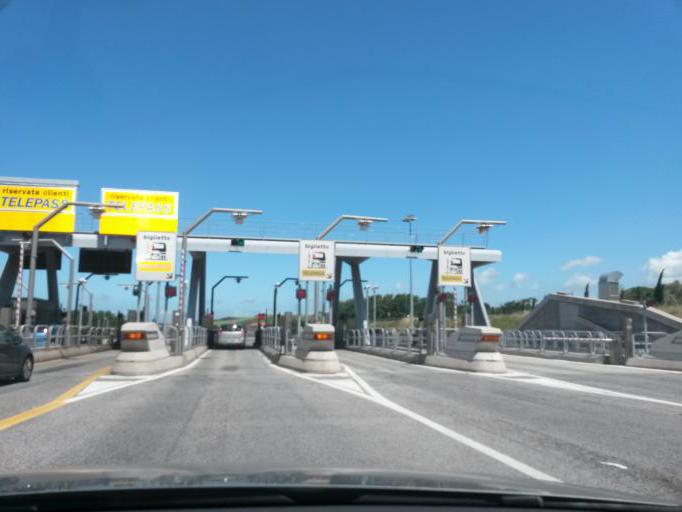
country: IT
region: Tuscany
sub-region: Provincia di Livorno
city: S.P. in Palazzi
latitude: 43.3690
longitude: 10.5046
